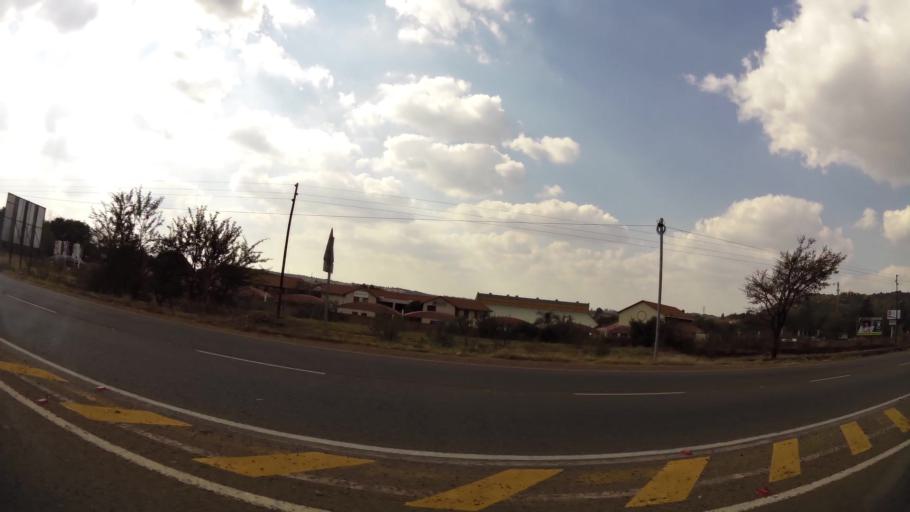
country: ZA
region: Gauteng
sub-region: City of Tshwane Metropolitan Municipality
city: Centurion
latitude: -25.8068
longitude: 28.3274
